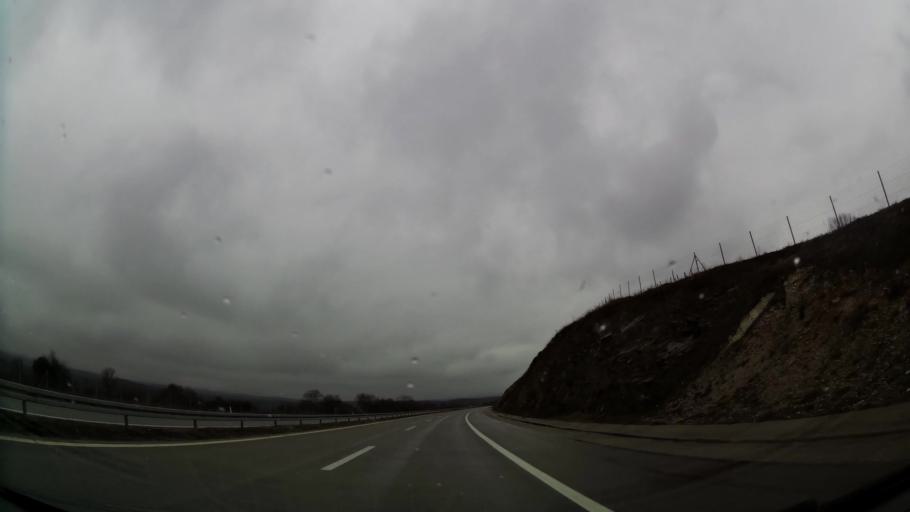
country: RS
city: Lagja e Poshtme
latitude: 42.3935
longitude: 21.7188
